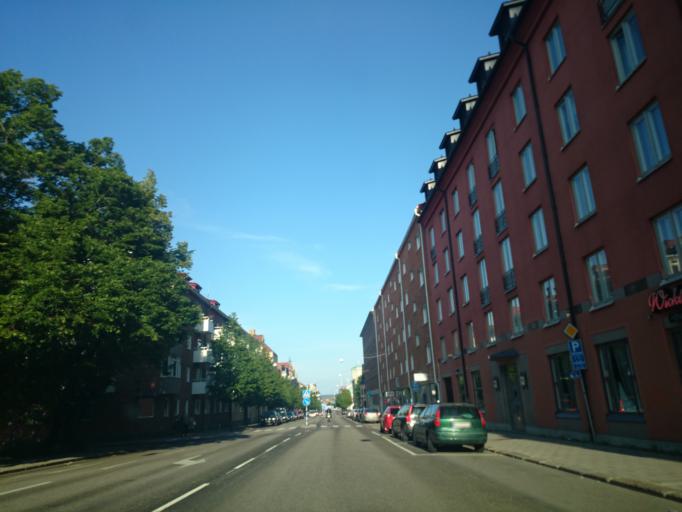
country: SE
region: Vaesternorrland
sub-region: Sundsvalls Kommun
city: Sundsvall
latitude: 62.3895
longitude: 17.3010
